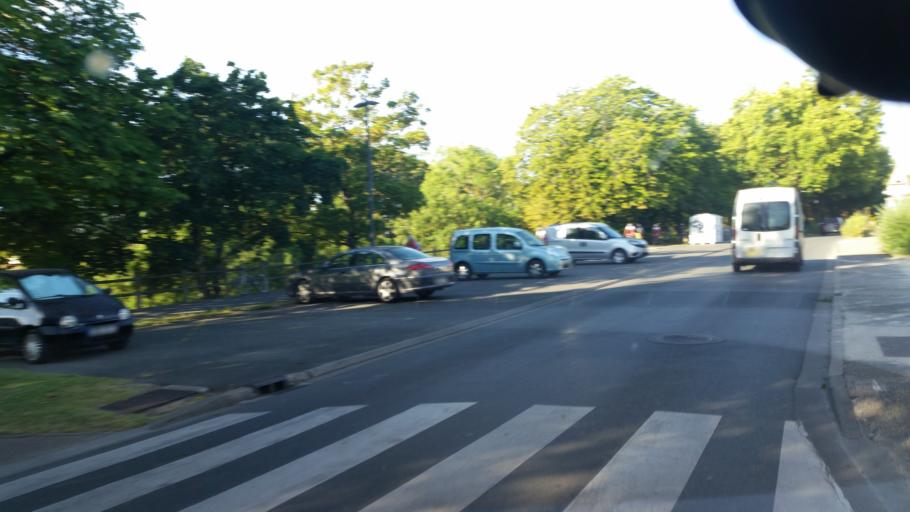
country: FR
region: Poitou-Charentes
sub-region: Departement de la Charente-Maritime
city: Perigny
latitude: 46.1672
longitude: -1.1093
